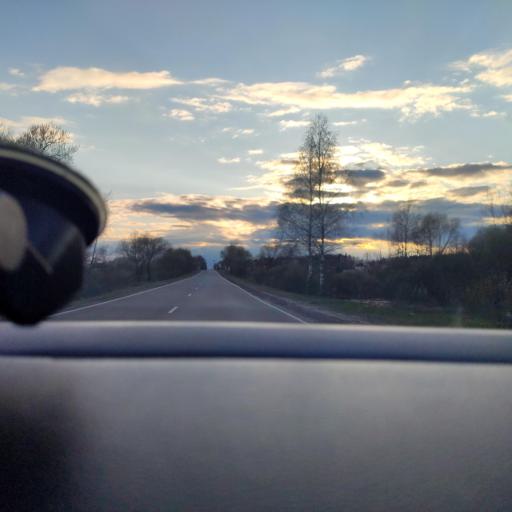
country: RU
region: Moskovskaya
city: Krasnyy Tkach
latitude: 55.4284
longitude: 39.2209
